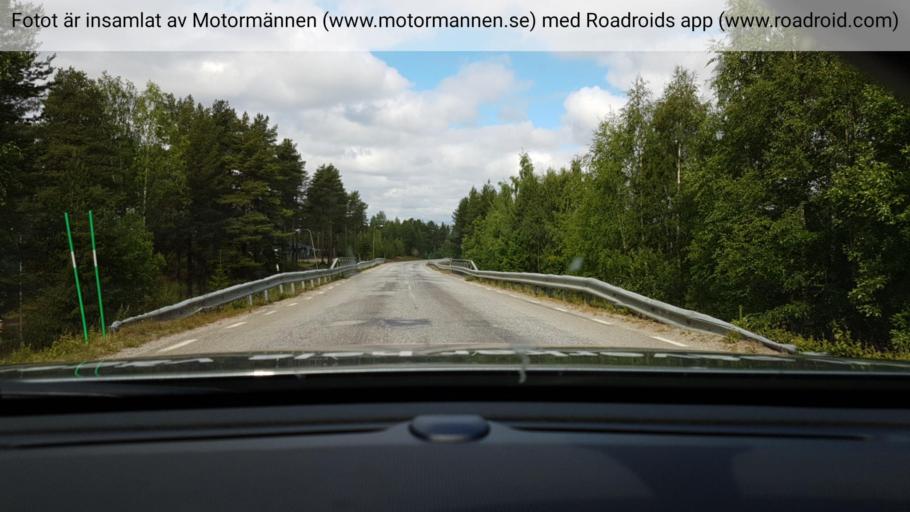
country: SE
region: Vaesterbotten
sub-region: Mala Kommun
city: Mala
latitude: 64.9032
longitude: 18.6939
